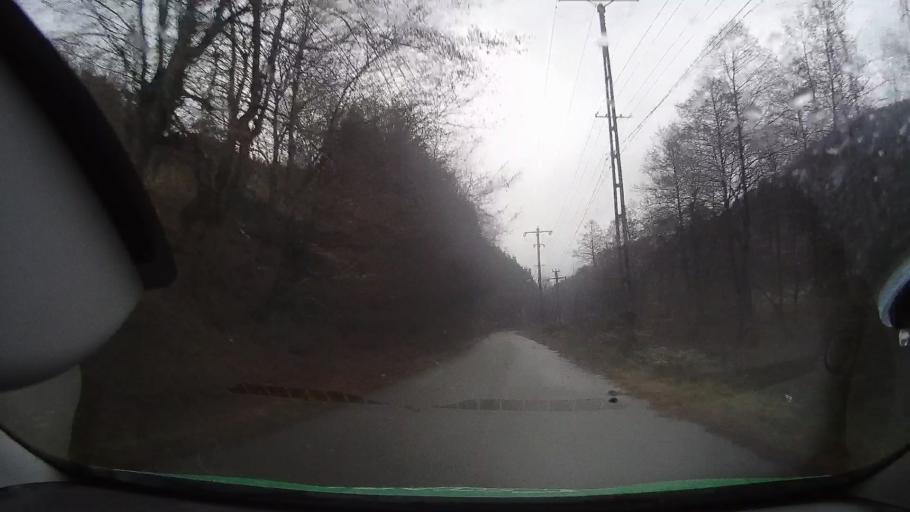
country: RO
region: Alba
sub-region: Comuna Avram Iancu
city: Avram Iancu
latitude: 46.2893
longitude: 22.7498
